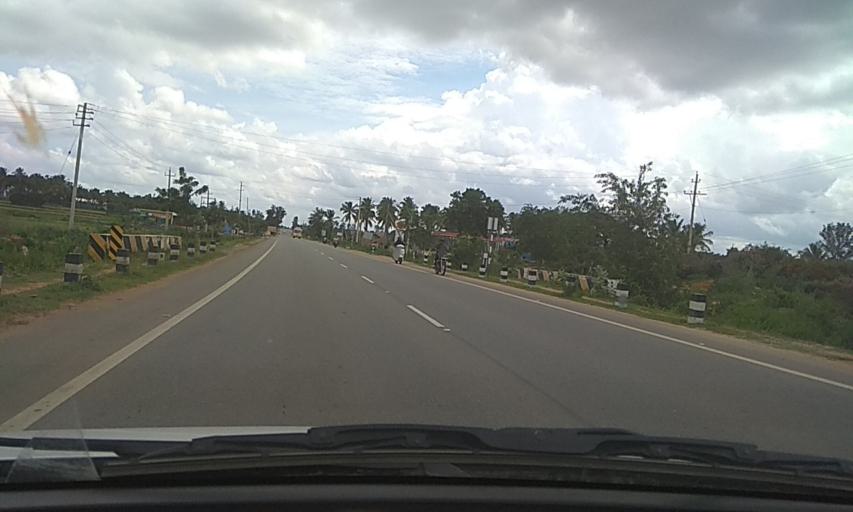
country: IN
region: Karnataka
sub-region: Tumkur
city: Tumkur
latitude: 13.2830
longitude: 77.0890
